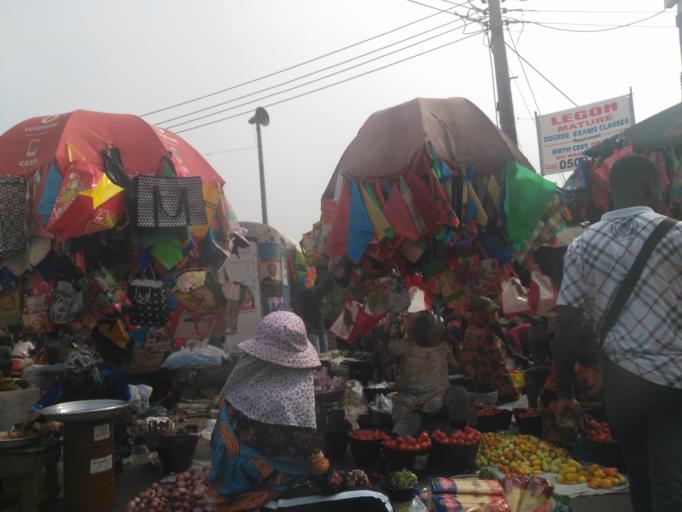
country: GH
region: Ashanti
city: Kumasi
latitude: 6.6993
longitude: -1.6196
